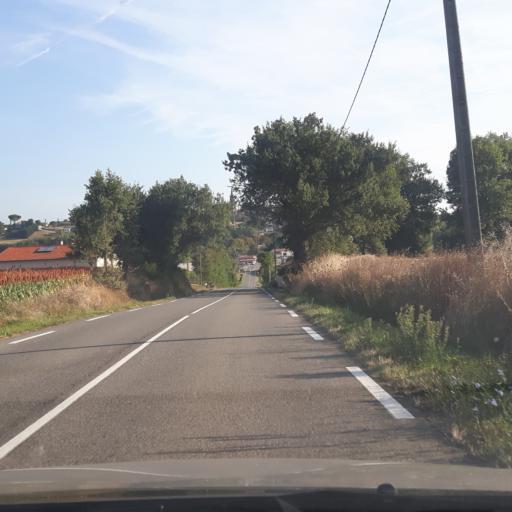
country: FR
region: Midi-Pyrenees
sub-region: Departement de la Haute-Garonne
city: Montjoire
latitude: 43.7632
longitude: 1.5268
